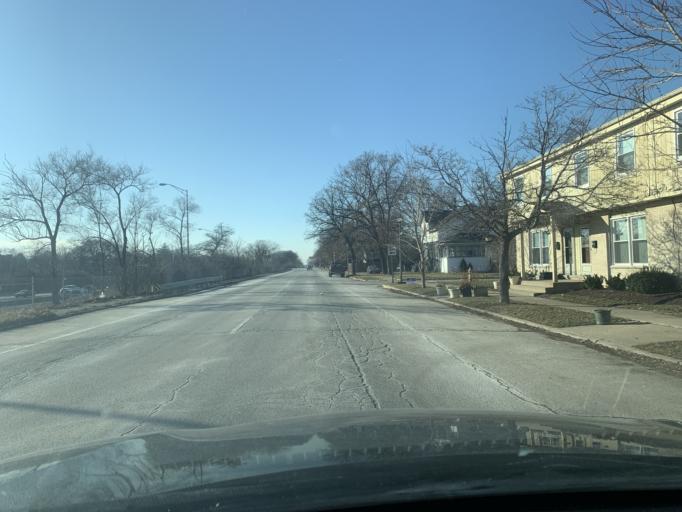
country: US
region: Illinois
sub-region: Cook County
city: Maywood
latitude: 41.8718
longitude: -87.8356
